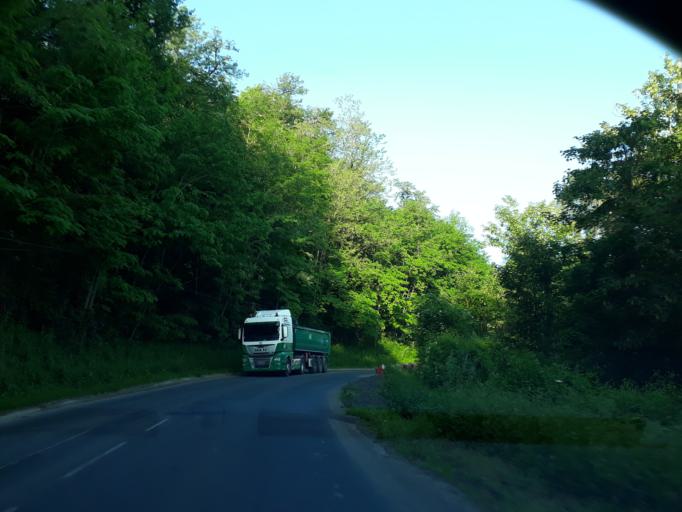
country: FR
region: Limousin
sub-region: Departement de la Correze
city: Saint-Pantaleon-de-Larche
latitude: 45.1329
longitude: 1.4720
